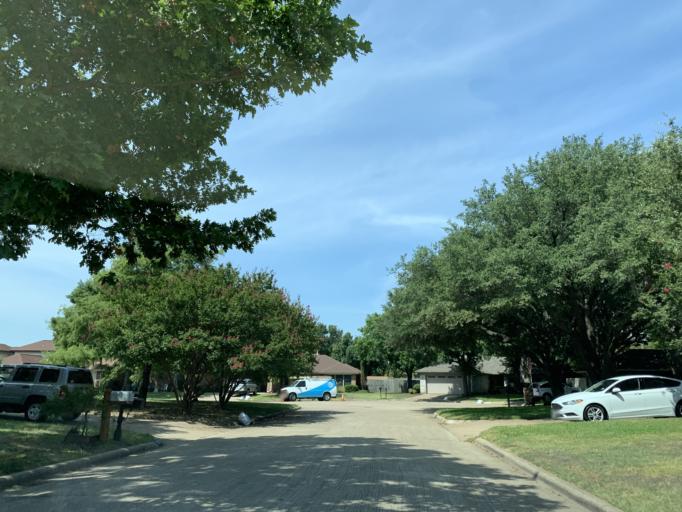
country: US
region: Texas
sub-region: Dallas County
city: Grand Prairie
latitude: 32.6676
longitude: -97.0424
